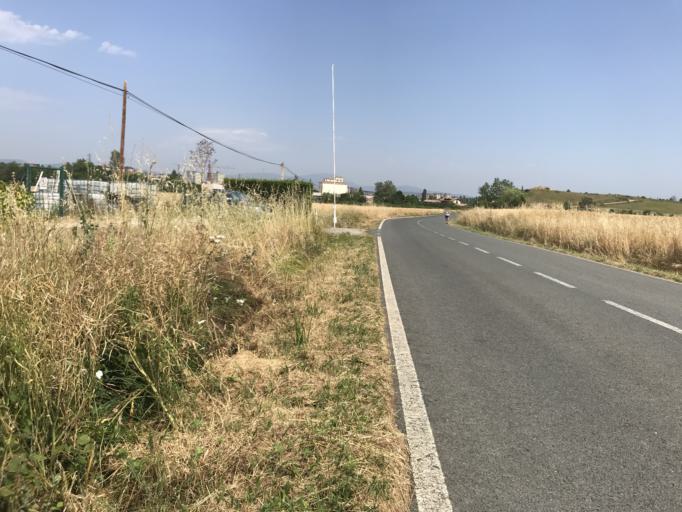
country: ES
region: Basque Country
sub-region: Provincia de Alava
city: Gasteiz / Vitoria
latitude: 42.8250
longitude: -2.6501
